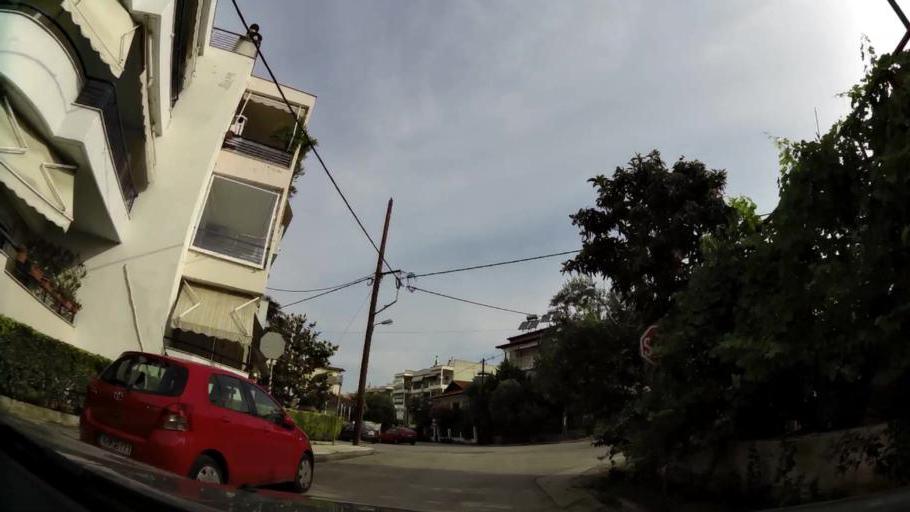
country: GR
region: Central Macedonia
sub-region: Nomos Thessalonikis
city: Thermi
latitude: 40.5458
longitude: 23.0170
